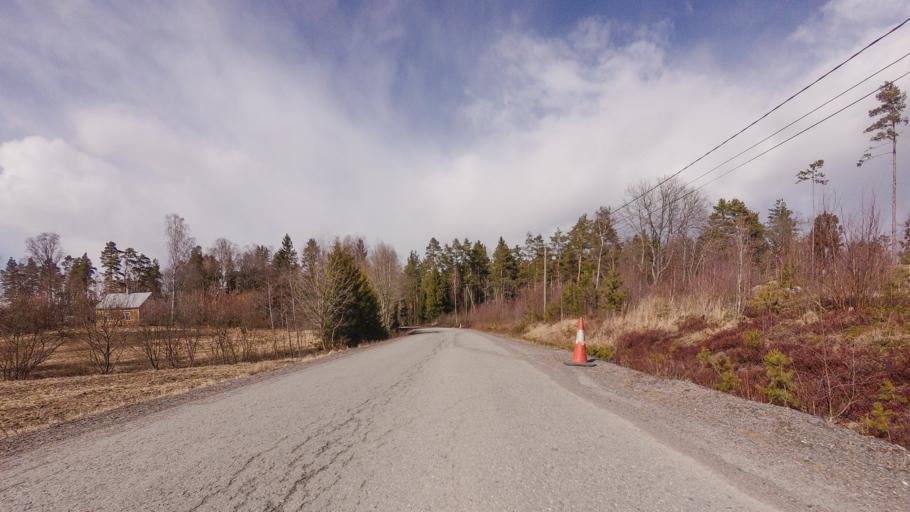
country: FI
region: Uusimaa
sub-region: Helsinki
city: Karjalohja
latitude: 60.3103
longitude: 23.7457
